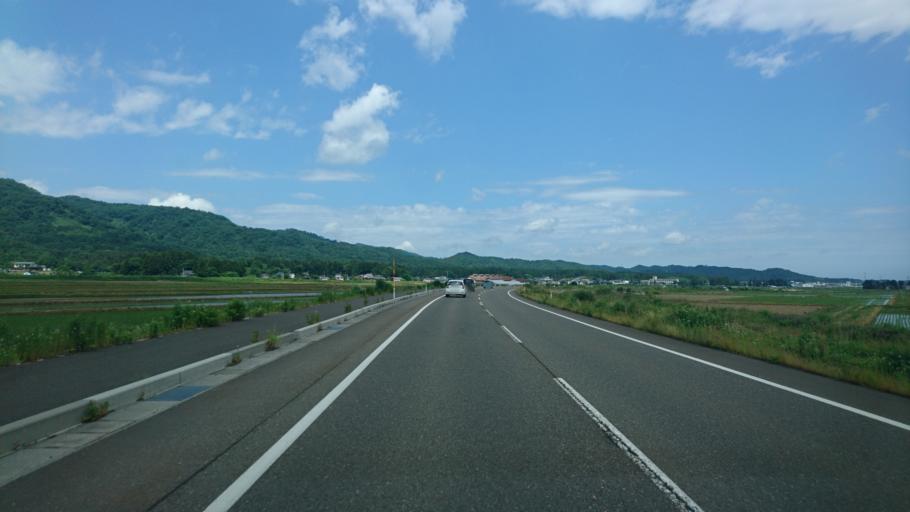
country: JP
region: Niigata
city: Arai
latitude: 37.0722
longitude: 138.2369
